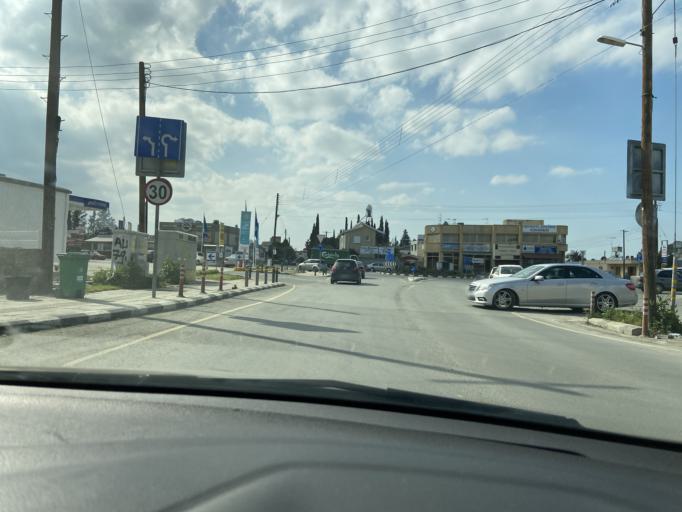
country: CY
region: Lefkosia
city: Alampra
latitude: 35.0145
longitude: 33.3949
